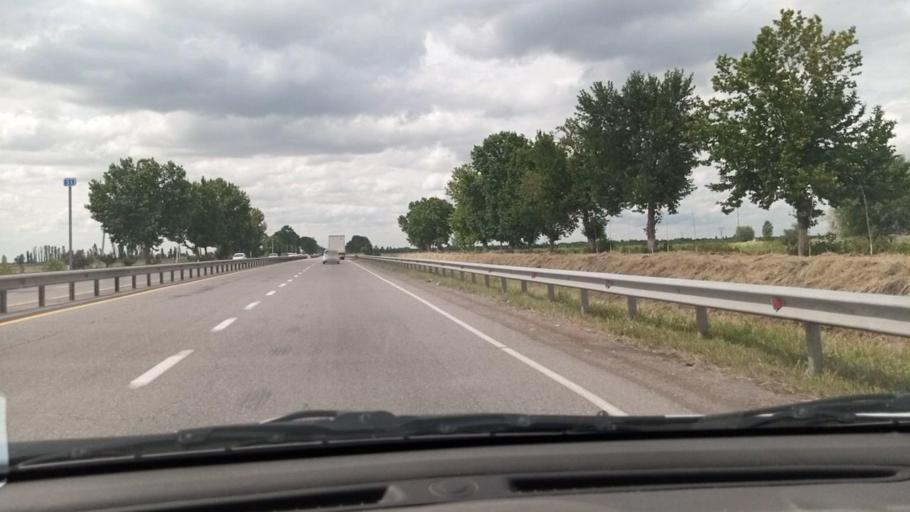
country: UZ
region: Toshkent Shahri
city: Bektemir
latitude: 41.1606
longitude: 69.4210
